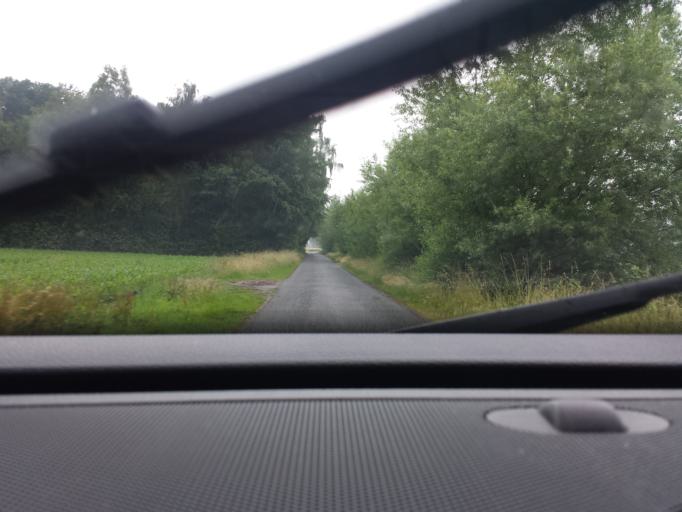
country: DE
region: North Rhine-Westphalia
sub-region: Regierungsbezirk Munster
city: Ahaus
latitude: 52.0720
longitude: 6.9526
